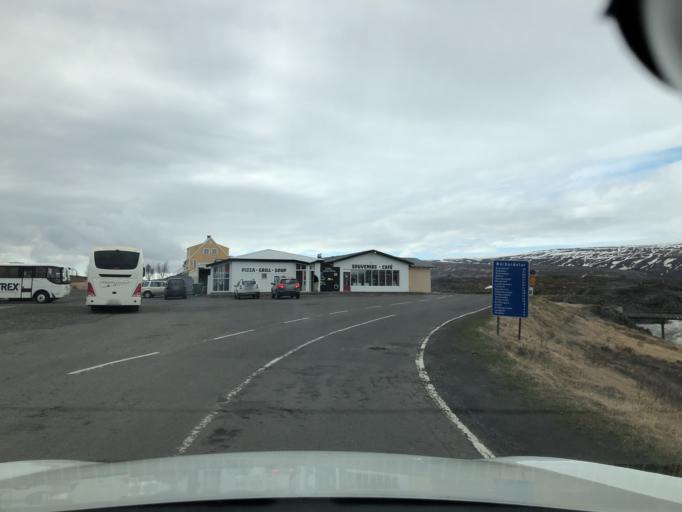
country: IS
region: Northeast
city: Laugar
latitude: 65.6863
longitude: -17.5391
